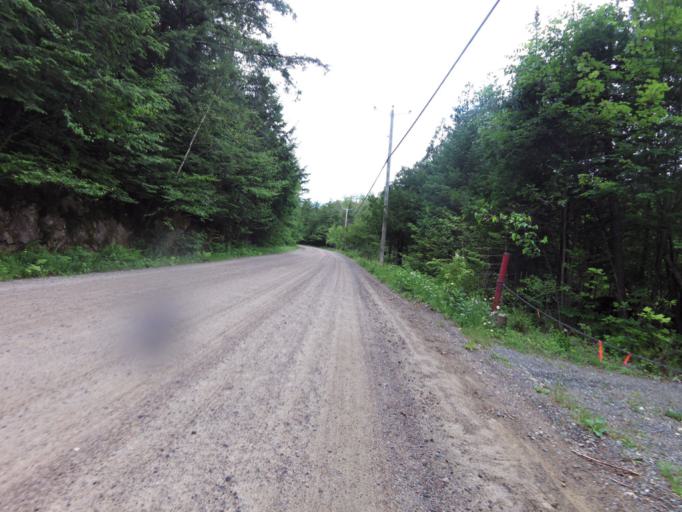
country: CA
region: Quebec
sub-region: Laurentides
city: Brownsburg-Chatham
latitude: 45.8506
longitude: -74.5714
